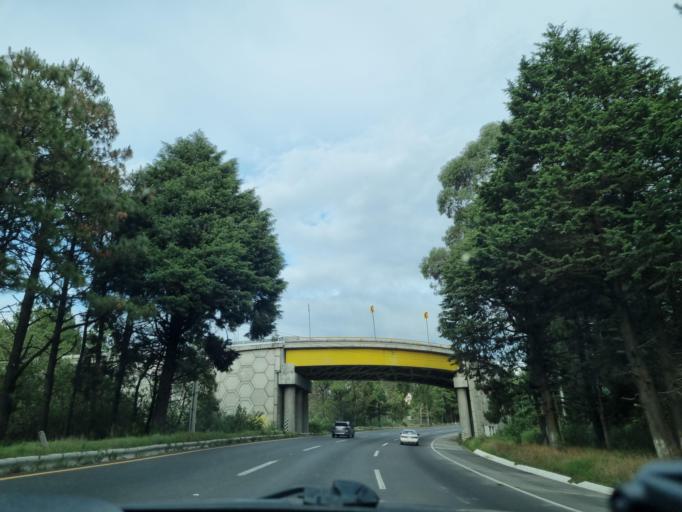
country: MX
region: Morelos
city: San Jeronimo Acazulco
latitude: 19.2977
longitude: -99.4030
